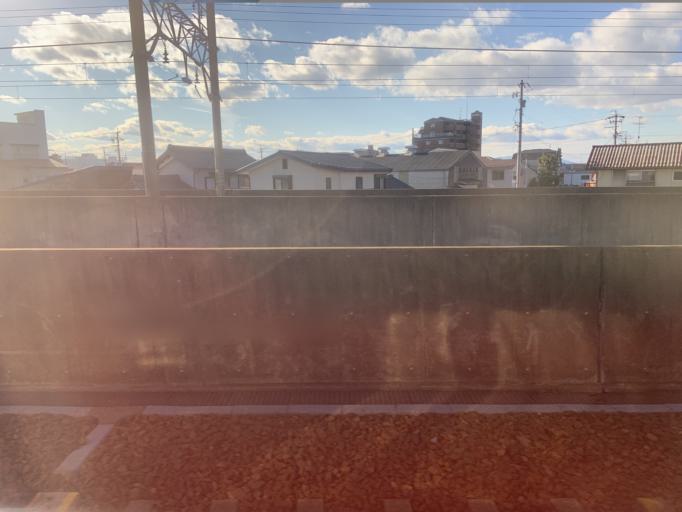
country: JP
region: Aichi
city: Ichinomiya
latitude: 35.3098
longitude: 136.7936
